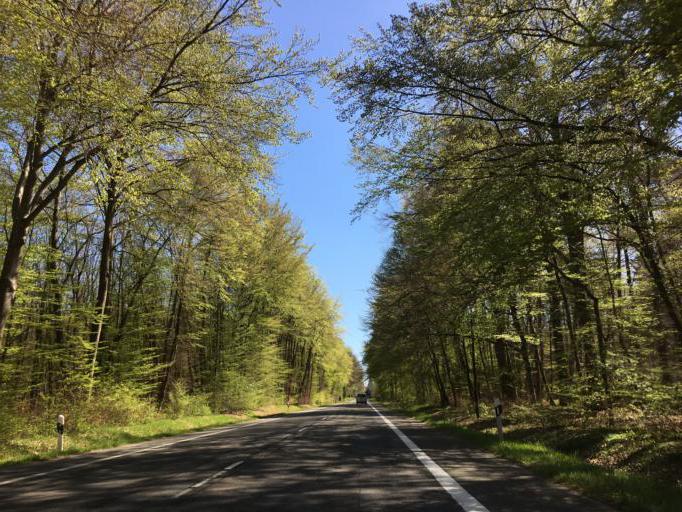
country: DE
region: Hesse
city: Langen
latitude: 50.0238
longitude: 8.6509
